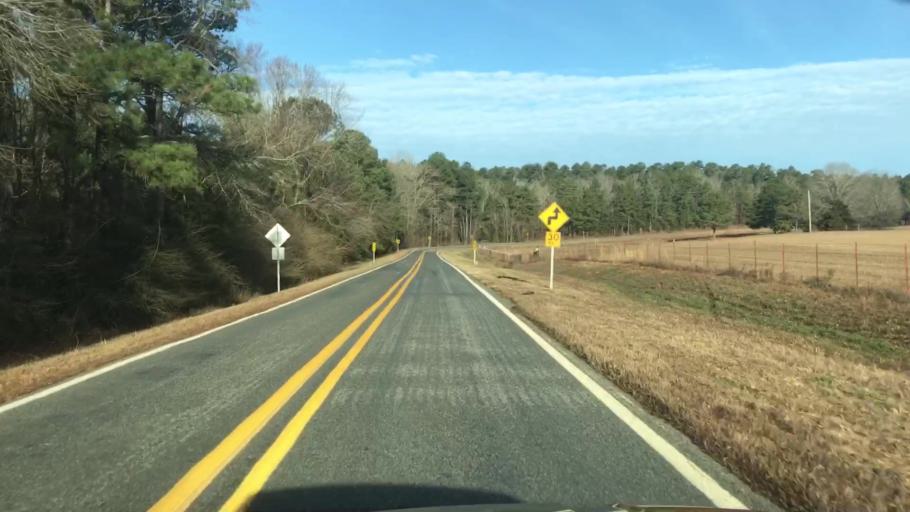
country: US
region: Arkansas
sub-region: Garland County
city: Rockwell
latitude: 34.4797
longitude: -93.2714
